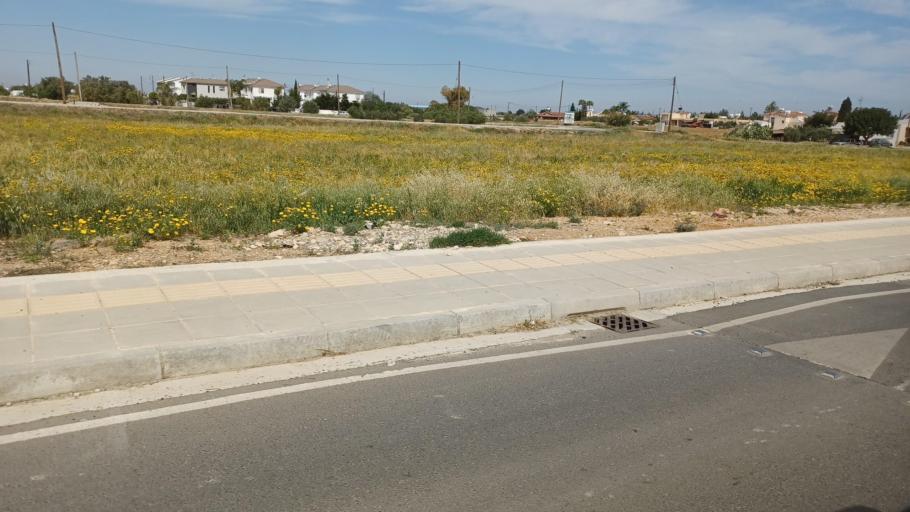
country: CY
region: Lefkosia
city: Kokkinotrimithia
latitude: 35.1565
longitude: 33.2055
